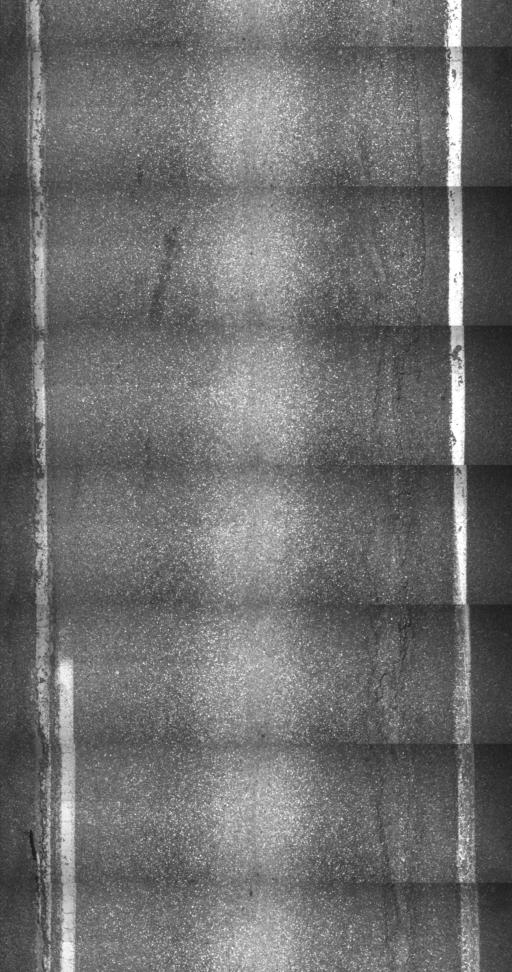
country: US
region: Vermont
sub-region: Chittenden County
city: Williston
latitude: 44.4115
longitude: -73.1248
